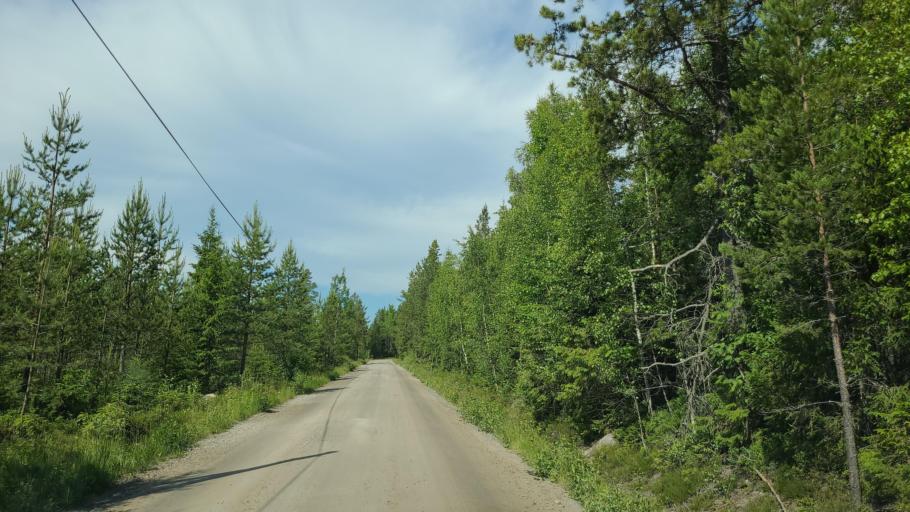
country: SE
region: Vaesterbotten
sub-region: Robertsfors Kommun
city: Robertsfors
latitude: 64.1557
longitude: 20.9456
